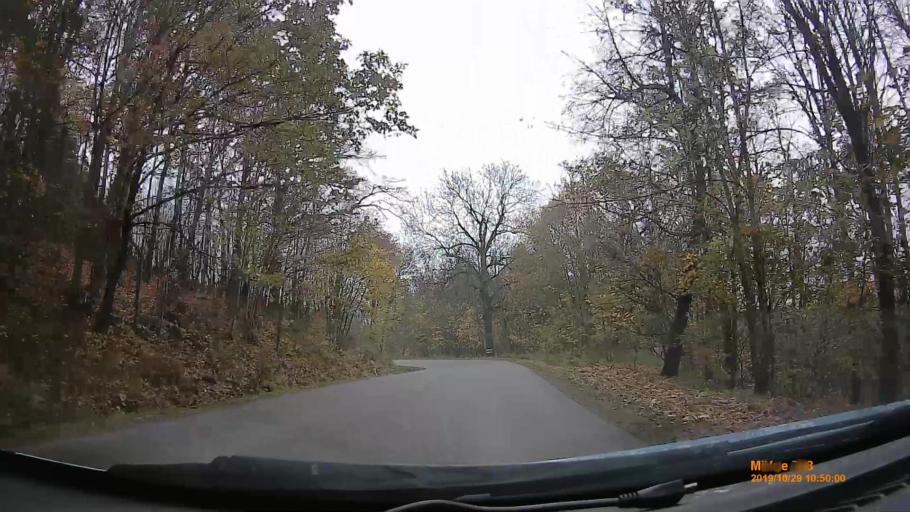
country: PL
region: Lower Silesian Voivodeship
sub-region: Powiat klodzki
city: Nowa Ruda
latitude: 50.5484
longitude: 16.4604
